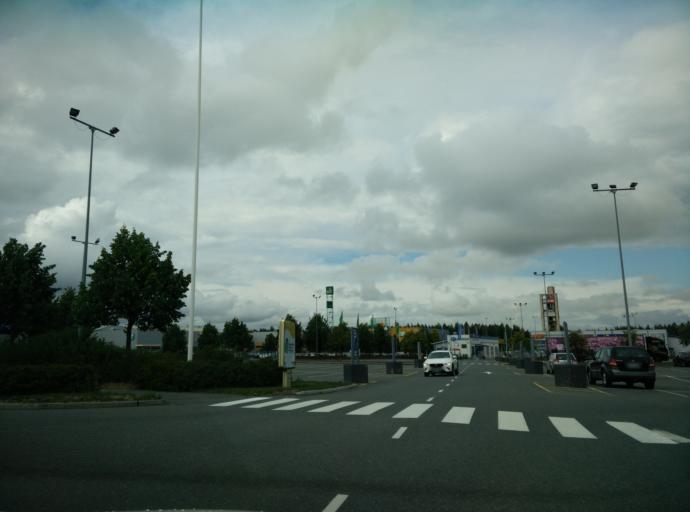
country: FI
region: Haeme
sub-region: Haemeenlinna
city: Haemeenlinna
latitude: 61.0074
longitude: 24.4201
